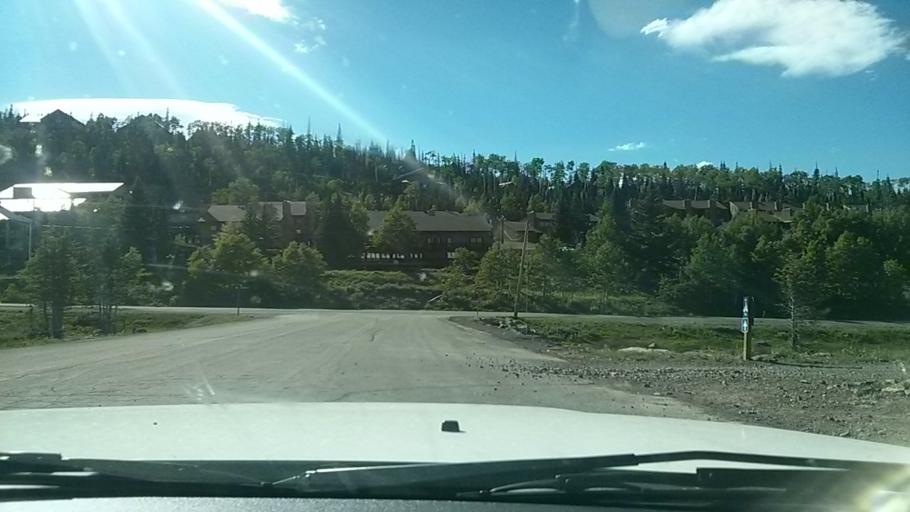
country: US
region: Utah
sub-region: Iron County
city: Parowan
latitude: 37.6941
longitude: -112.8469
